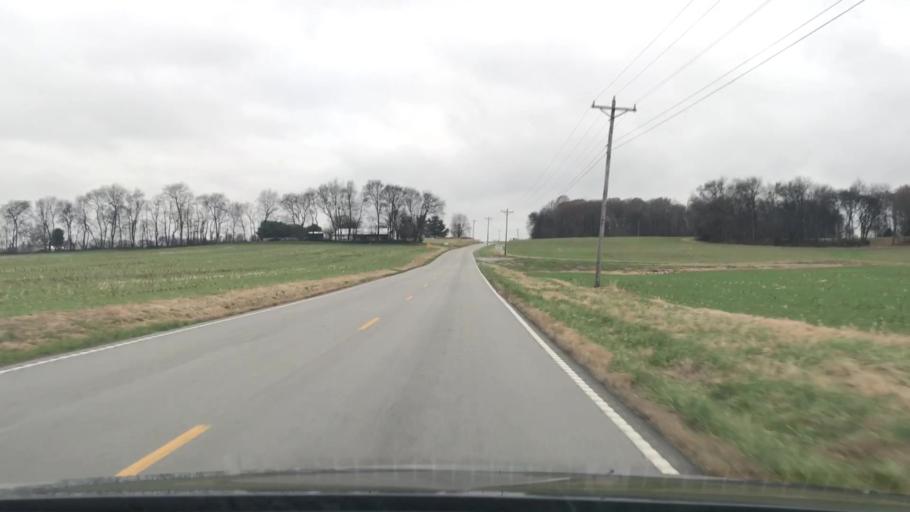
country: US
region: Kentucky
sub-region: Todd County
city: Guthrie
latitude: 36.6816
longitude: -87.2002
